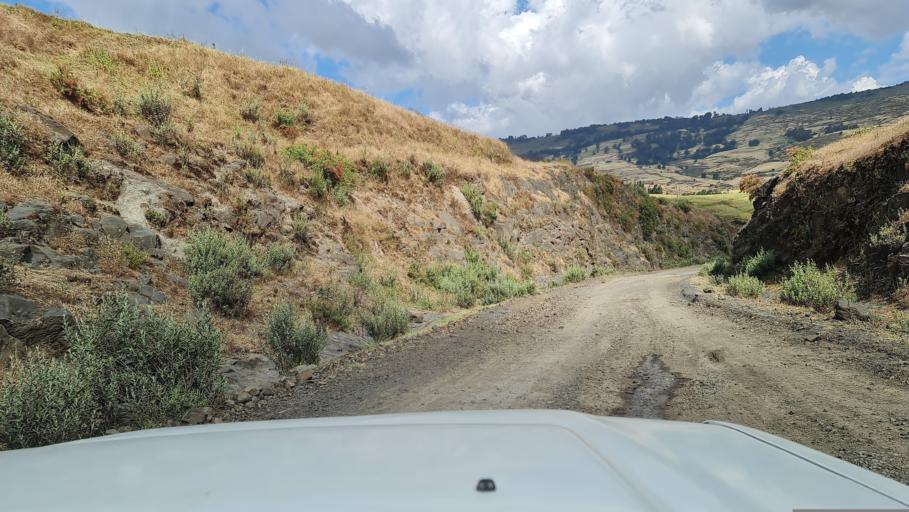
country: ET
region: Amhara
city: Debark'
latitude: 13.1329
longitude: 37.9268
